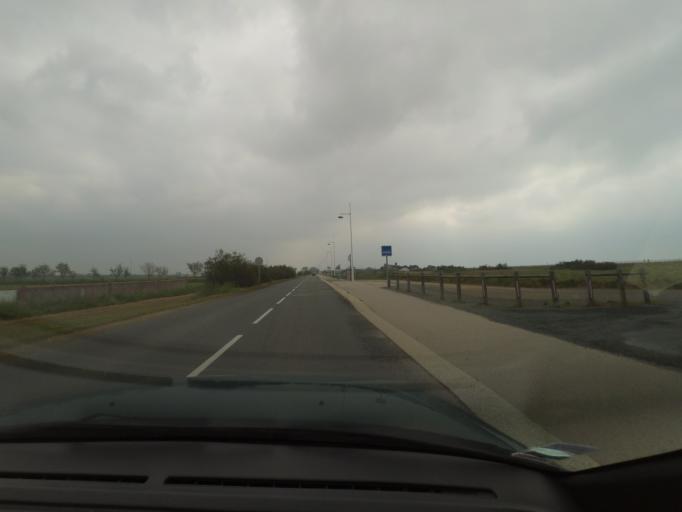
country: FR
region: Pays de la Loire
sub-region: Departement de la Vendee
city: Angles
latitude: 46.3431
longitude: -1.3432
